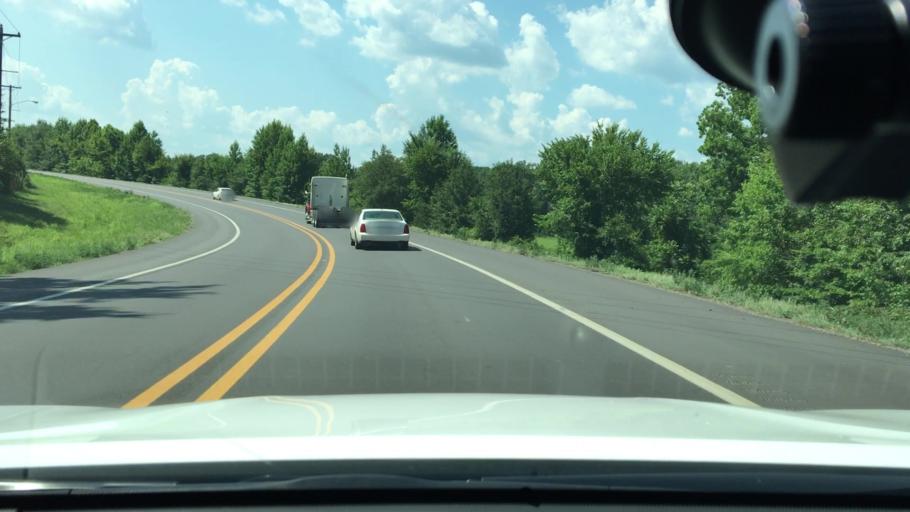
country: US
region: Arkansas
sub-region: Johnson County
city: Clarksville
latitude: 35.4514
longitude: -93.5294
